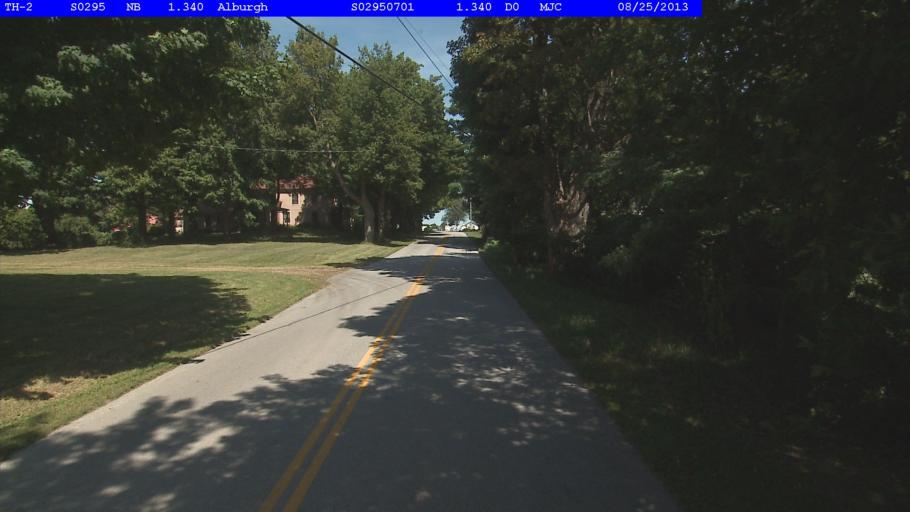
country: US
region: Vermont
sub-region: Franklin County
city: Swanton
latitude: 44.9927
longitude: -73.2226
